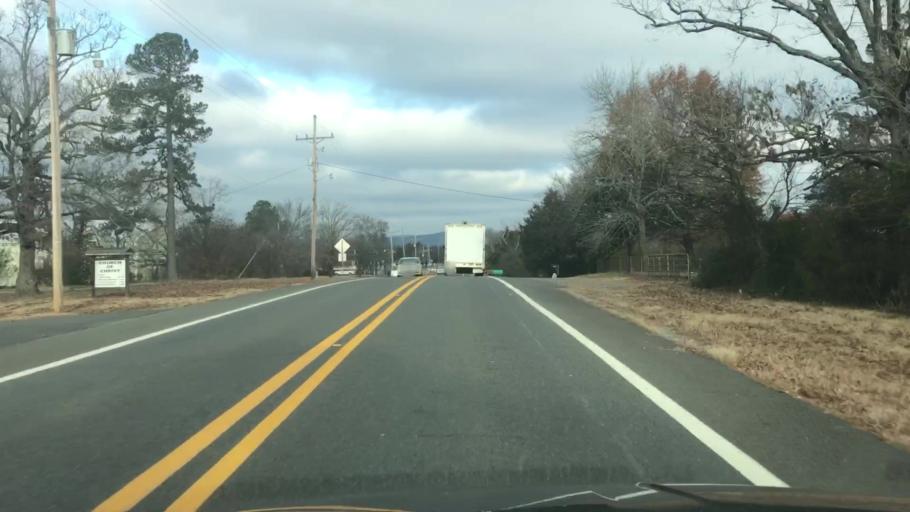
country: US
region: Arkansas
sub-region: Montgomery County
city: Mount Ida
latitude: 34.6266
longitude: -93.7313
